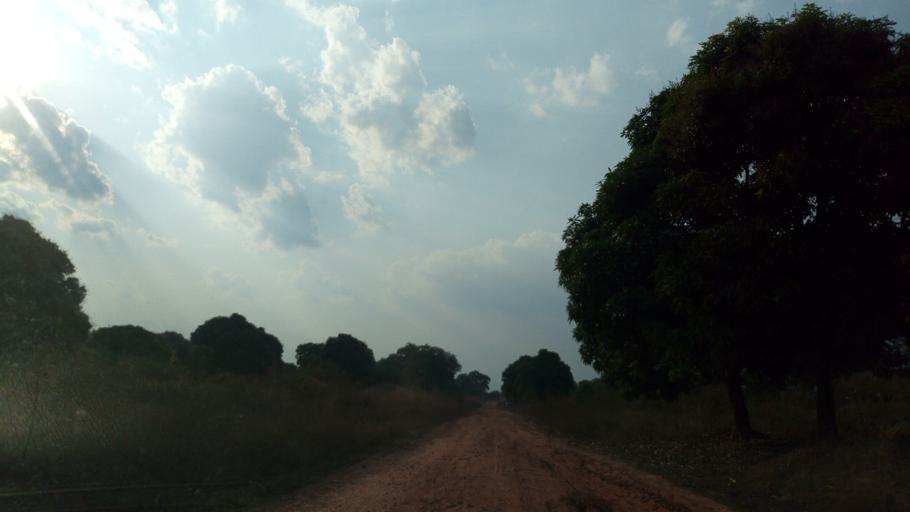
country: TZ
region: Kigoma
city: Kigoma
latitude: -5.1264
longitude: 28.9003
